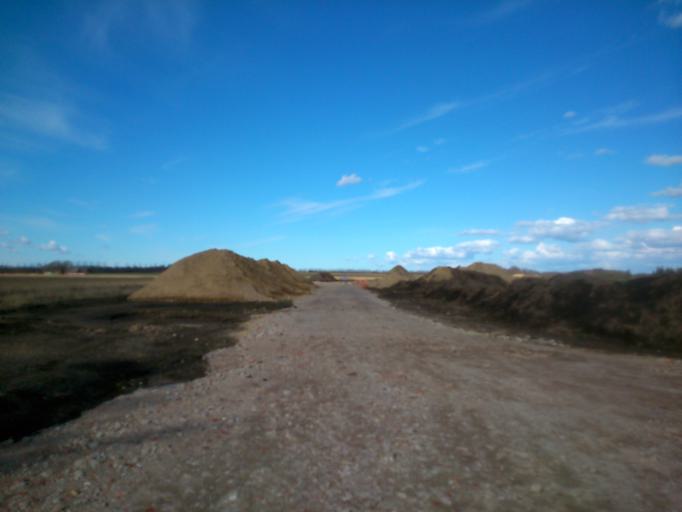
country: DK
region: Central Jutland
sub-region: Ringkobing-Skjern Kommune
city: Videbaek
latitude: 56.0172
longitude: 8.5767
